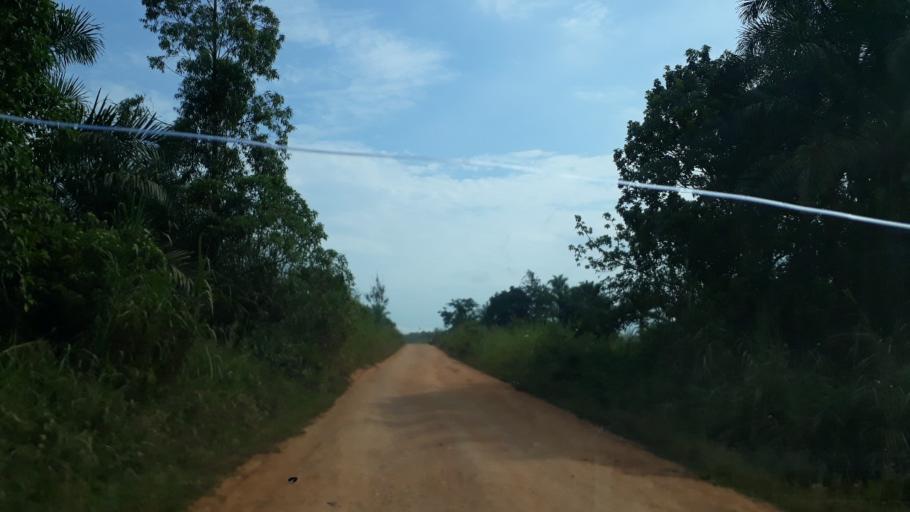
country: CD
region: Eastern Province
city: Bunia
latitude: 1.3834
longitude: 29.7934
